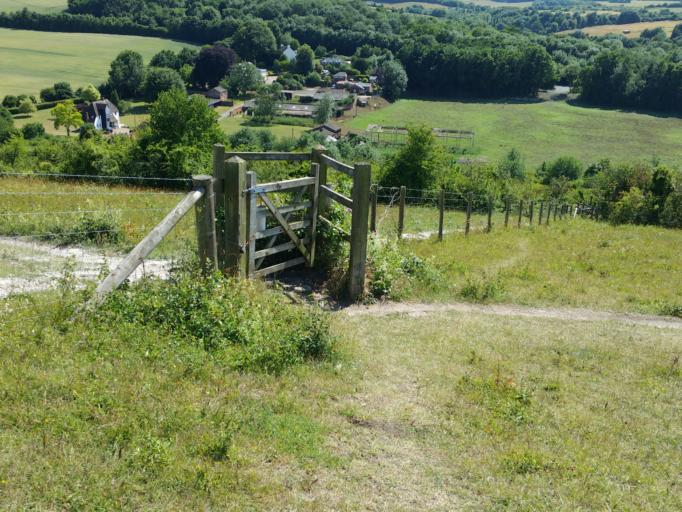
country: GB
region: England
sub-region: Kent
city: Gillingham
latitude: 51.3649
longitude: 0.5603
